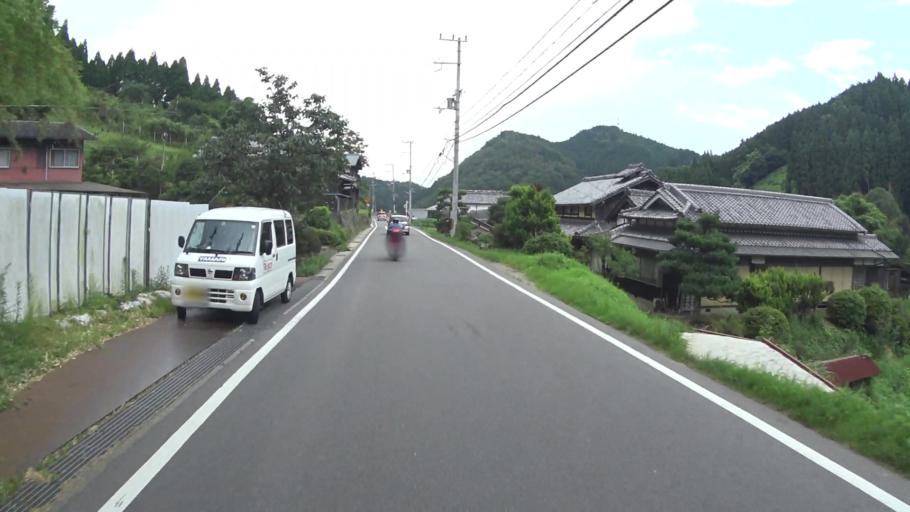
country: JP
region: Kyoto
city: Uji
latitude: 34.8573
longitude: 135.9221
